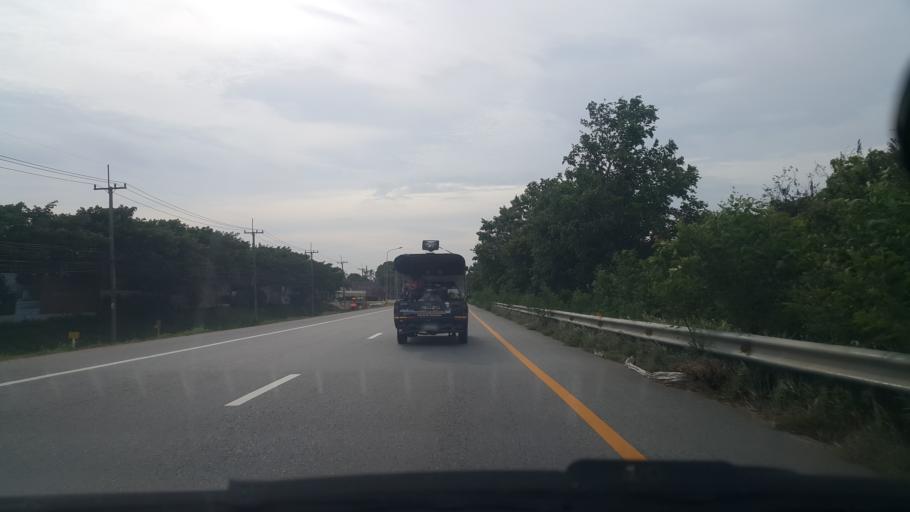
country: TH
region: Chon Buri
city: Bang Lamung
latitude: 12.9726
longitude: 100.9692
